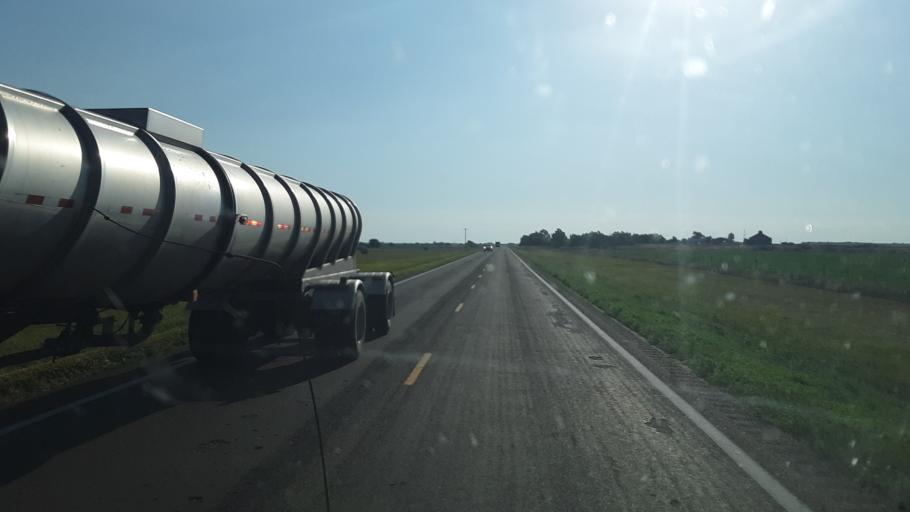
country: US
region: Kansas
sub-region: Edwards County
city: Kinsley
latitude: 38.1735
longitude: -99.5835
